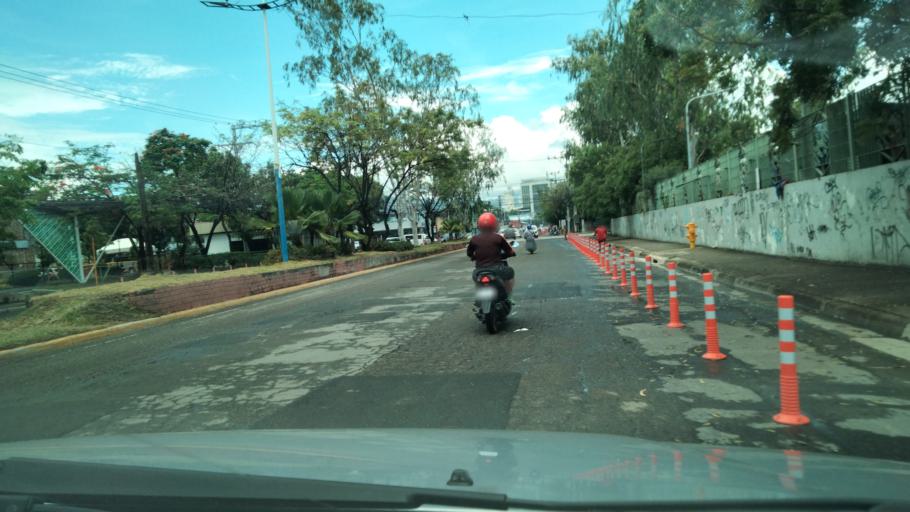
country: PH
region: Central Visayas
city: Mandaue City
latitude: 10.3261
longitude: 123.9352
